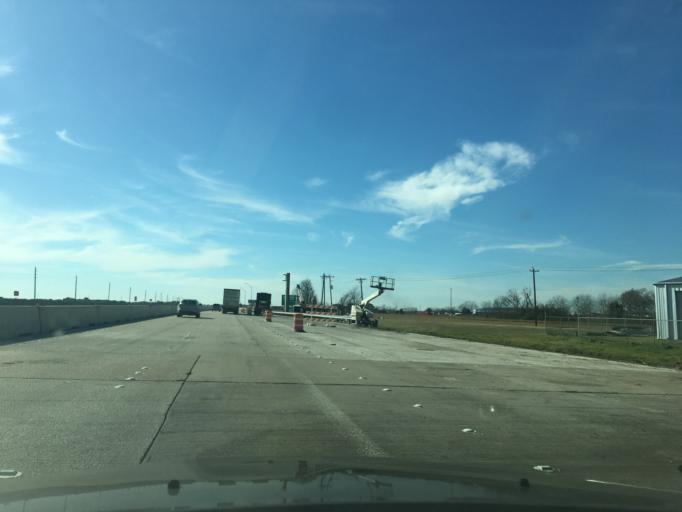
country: US
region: Texas
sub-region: Fort Bend County
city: Pleak
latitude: 29.4914
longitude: -95.9189
